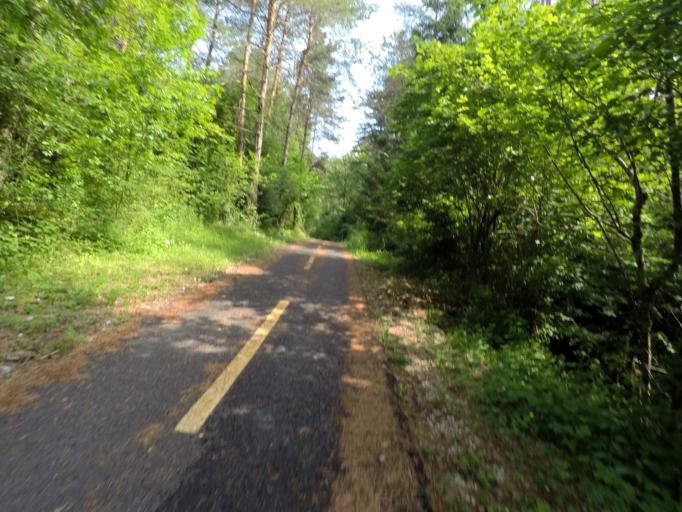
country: IT
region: Friuli Venezia Giulia
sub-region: Provincia di Udine
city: Cavazzo Carnico
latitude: 46.3737
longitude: 13.0333
